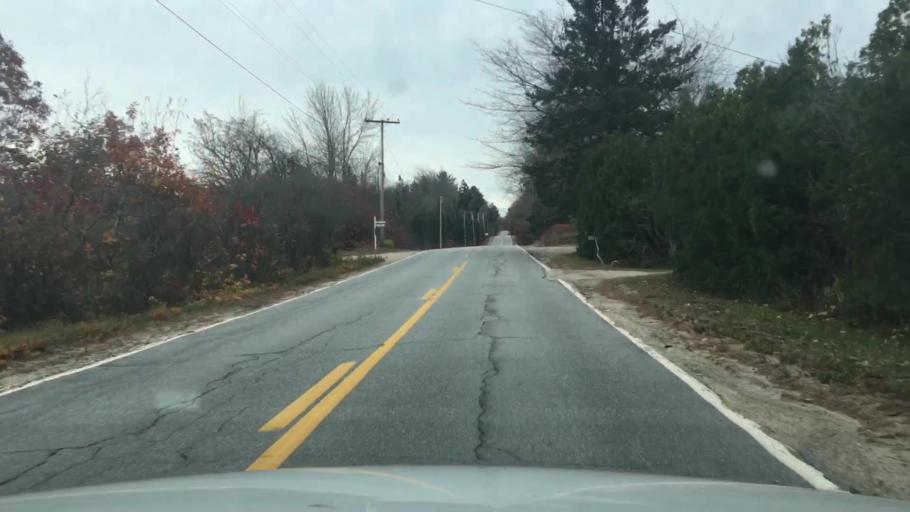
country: US
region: Maine
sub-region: Hancock County
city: Sedgwick
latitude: 44.3159
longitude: -68.5706
